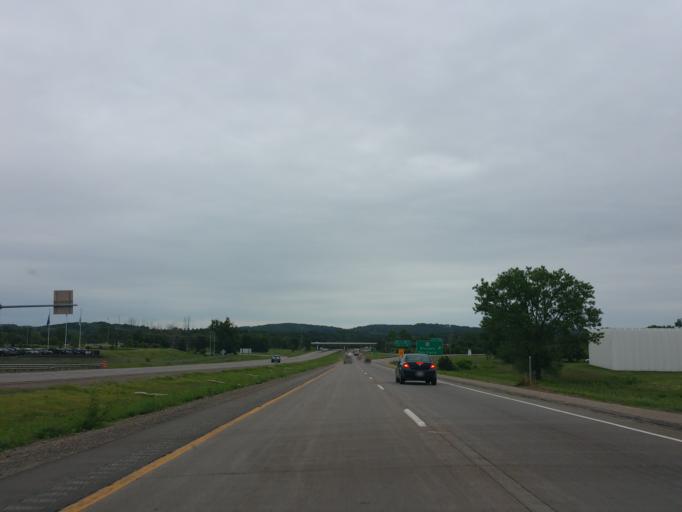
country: US
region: Wisconsin
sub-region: Eau Claire County
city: Altoona
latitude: 44.7660
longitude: -91.4316
